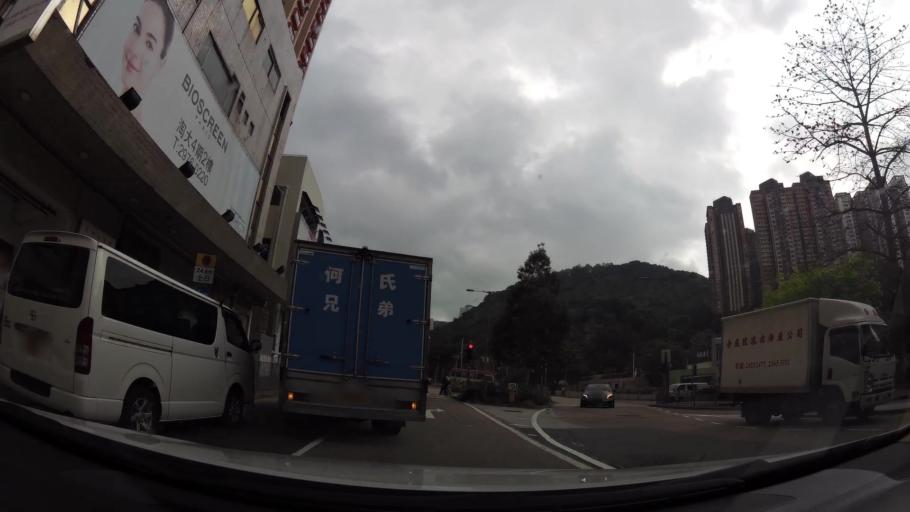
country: HK
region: Kowloon City
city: Kowloon
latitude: 22.3237
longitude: 114.2172
